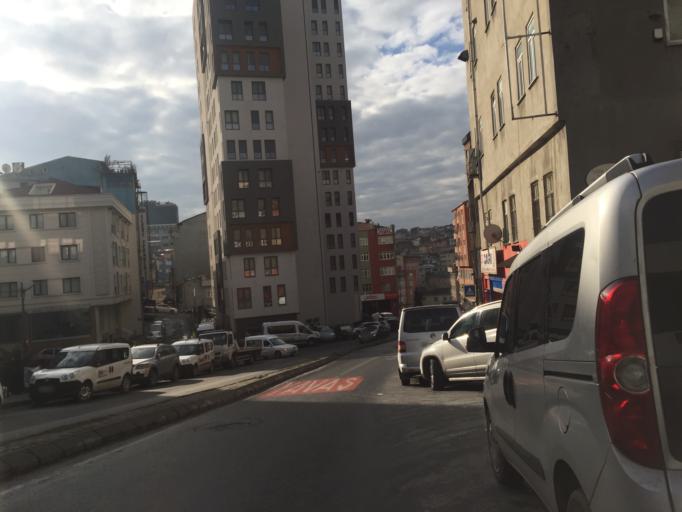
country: TR
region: Istanbul
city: Sisli
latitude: 41.0992
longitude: 28.9980
